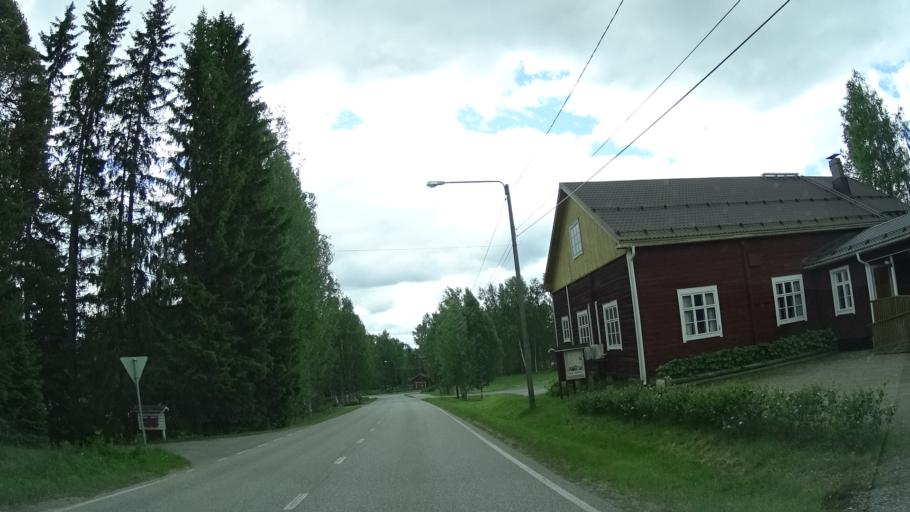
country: FI
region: Central Finland
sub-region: Jyvaeskylae
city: Toivakka
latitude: 61.9991
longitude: 25.9735
